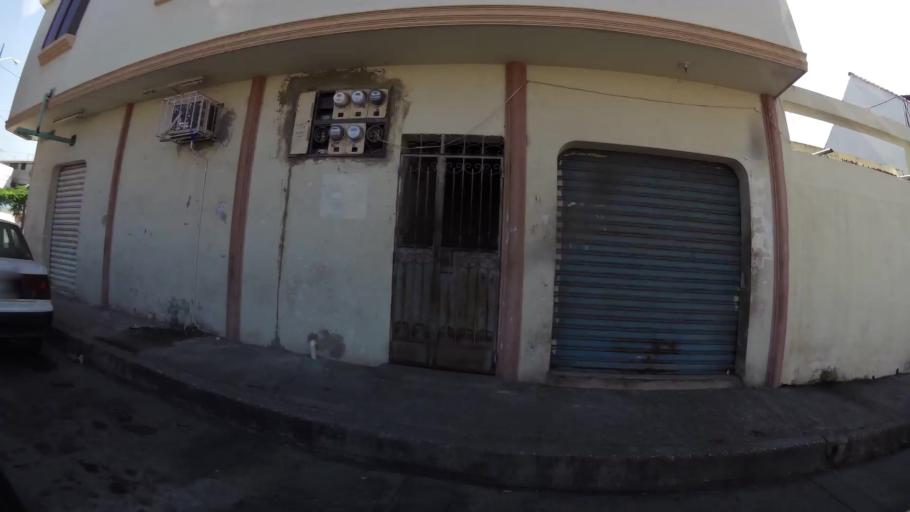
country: EC
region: Guayas
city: Eloy Alfaro
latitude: -2.1203
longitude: -79.8889
